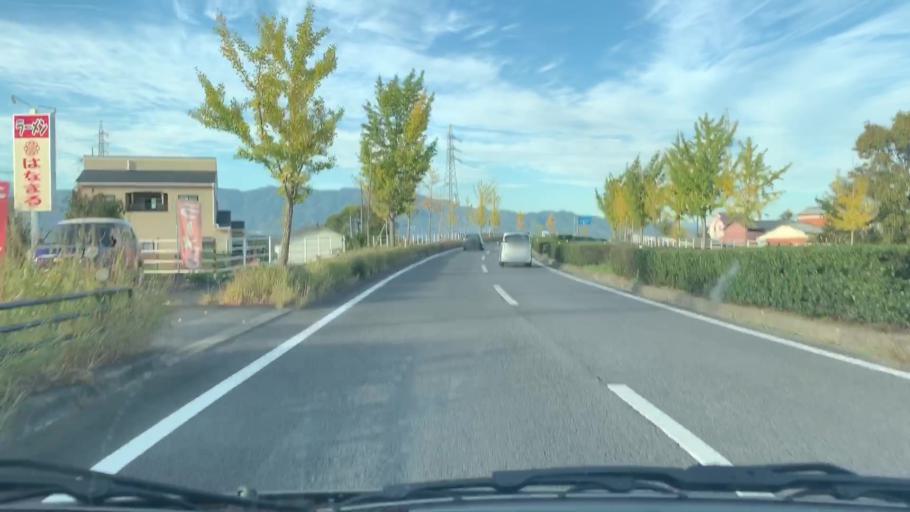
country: JP
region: Saga Prefecture
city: Saga-shi
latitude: 33.2540
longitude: 130.1992
